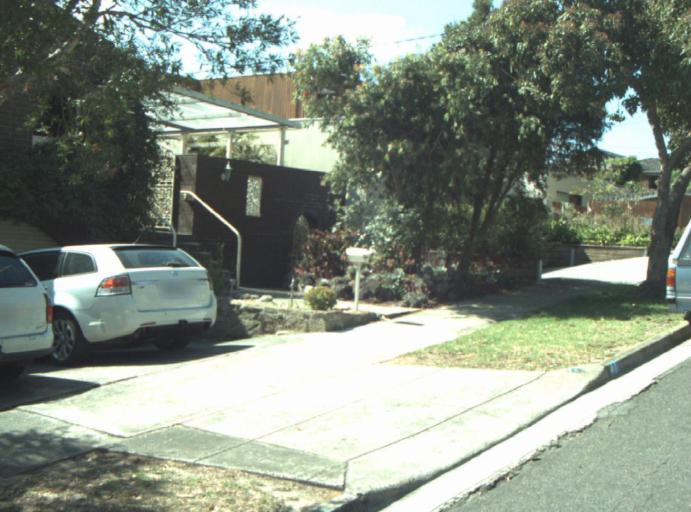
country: AU
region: Victoria
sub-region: Greater Geelong
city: Wandana Heights
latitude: -38.1639
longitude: 144.3231
